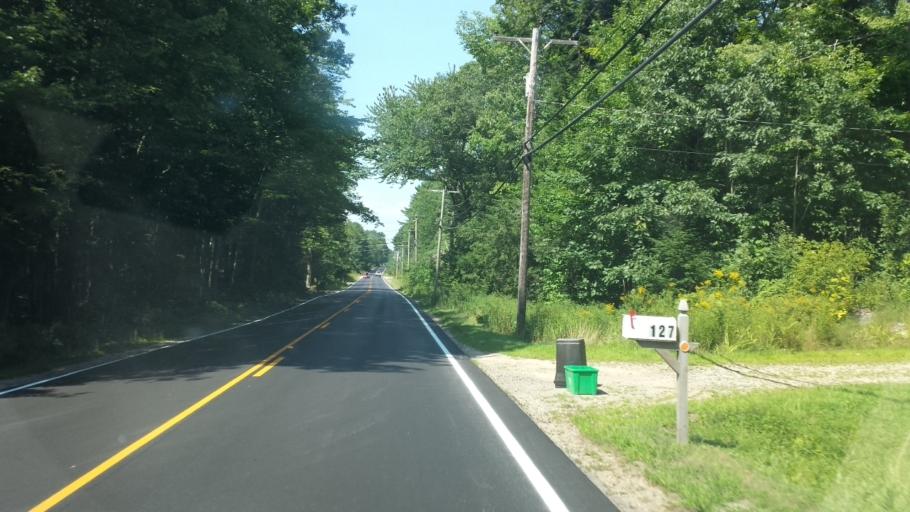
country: US
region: Maine
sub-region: York County
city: Arundel
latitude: 43.3983
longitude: -70.4853
